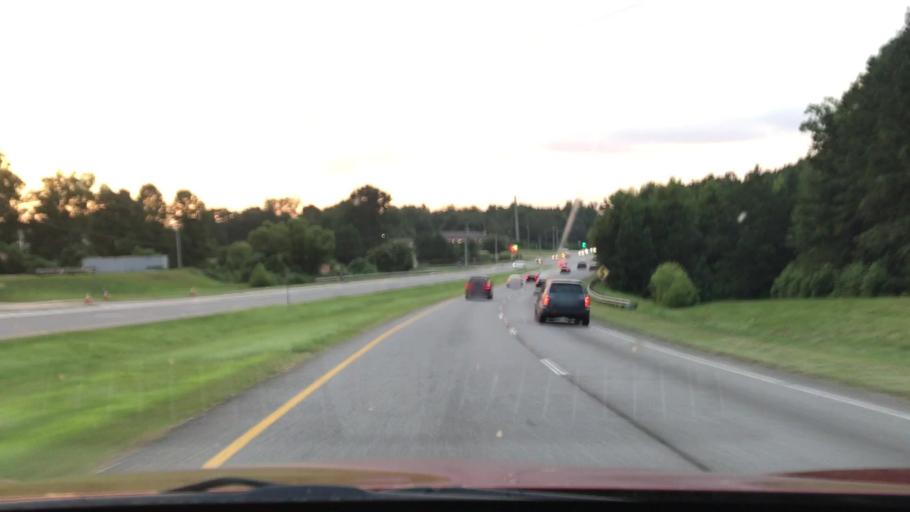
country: US
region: Georgia
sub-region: Gwinnett County
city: Sugar Hill
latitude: 34.0420
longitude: -83.9912
